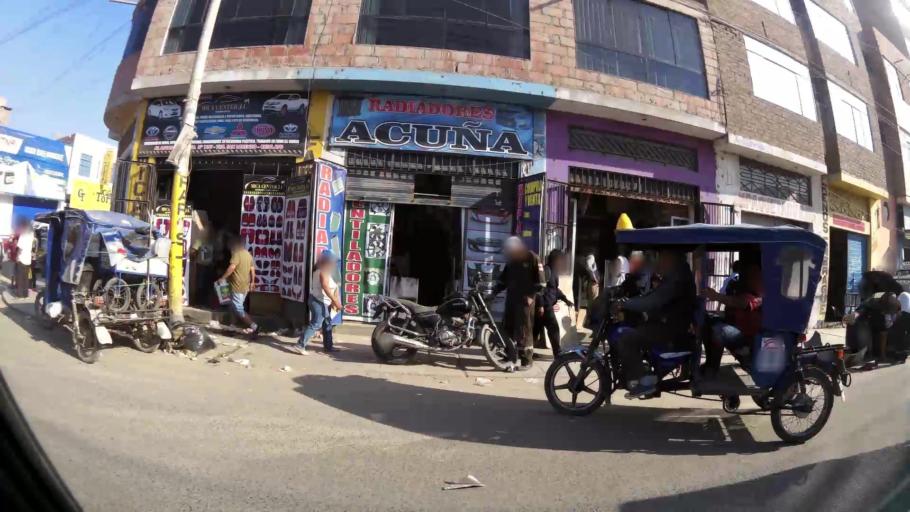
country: PE
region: Lambayeque
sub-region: Provincia de Chiclayo
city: Chiclayo
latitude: -6.7625
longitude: -79.8444
